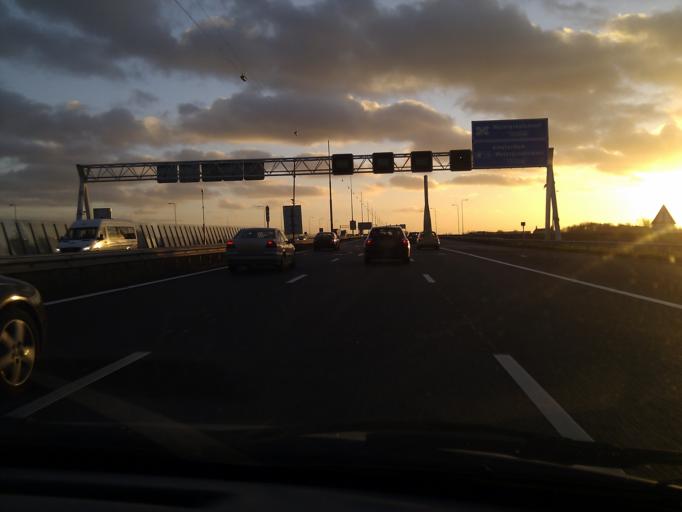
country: NL
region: North Holland
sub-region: Gemeente Diemen
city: Diemen
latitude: 52.3666
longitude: 4.9715
